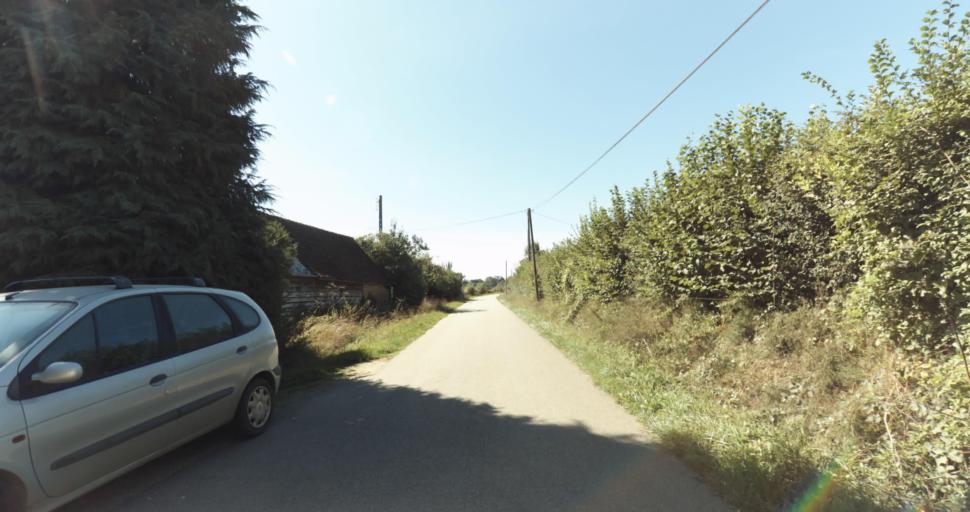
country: FR
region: Lower Normandy
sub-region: Departement de l'Orne
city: Gace
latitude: 48.7832
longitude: 0.2799
